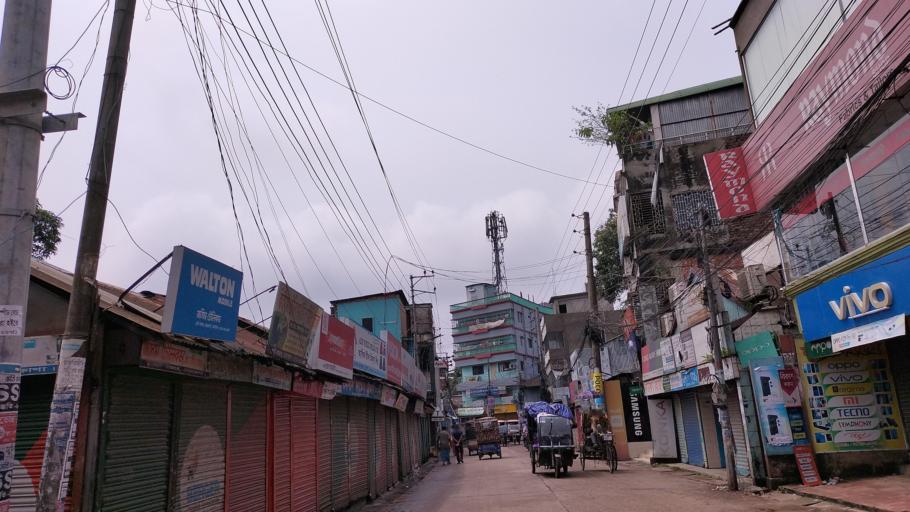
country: BD
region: Dhaka
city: Netrakona
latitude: 24.8842
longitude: 90.7325
